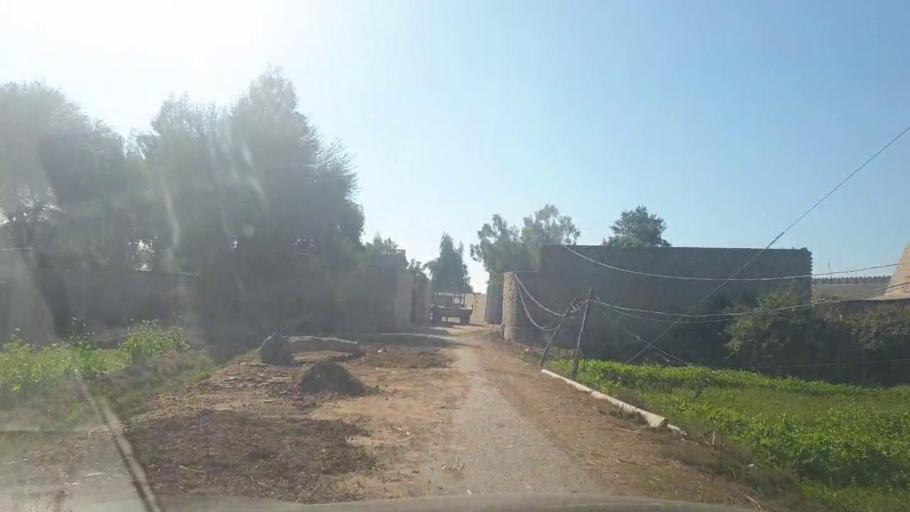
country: PK
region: Sindh
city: Adilpur
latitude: 27.9709
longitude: 69.3341
